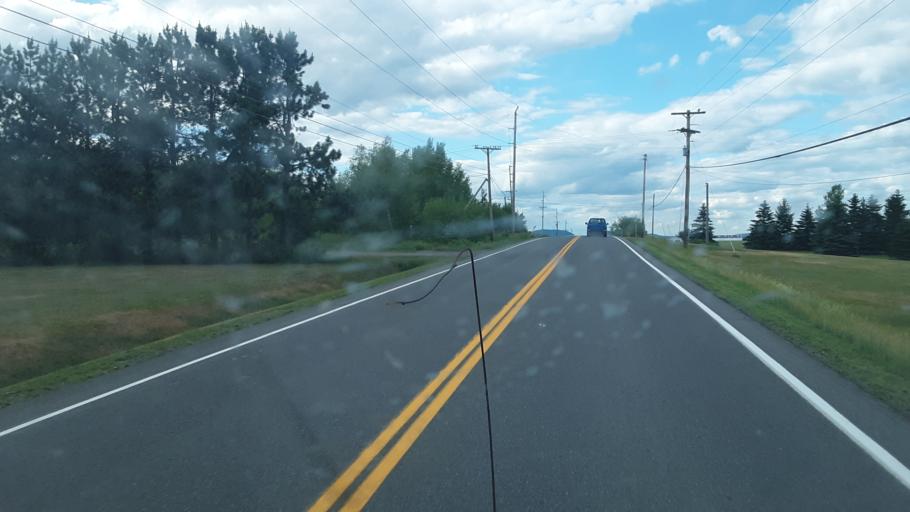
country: US
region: Maine
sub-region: Penobscot County
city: Patten
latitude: 45.9793
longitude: -68.4501
